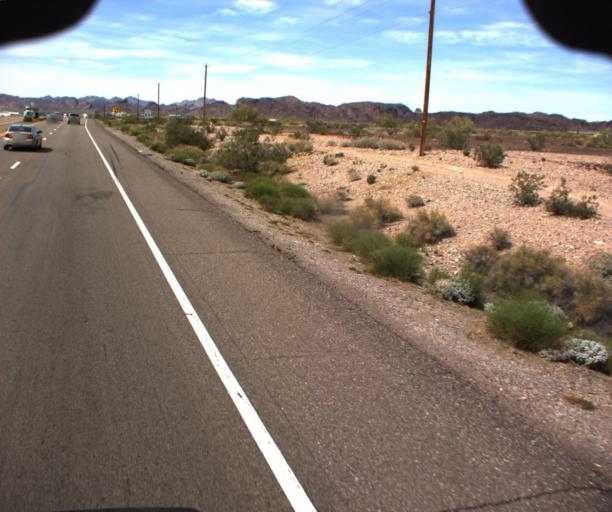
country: US
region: Arizona
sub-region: Mohave County
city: Desert Hills
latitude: 34.5474
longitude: -114.3554
